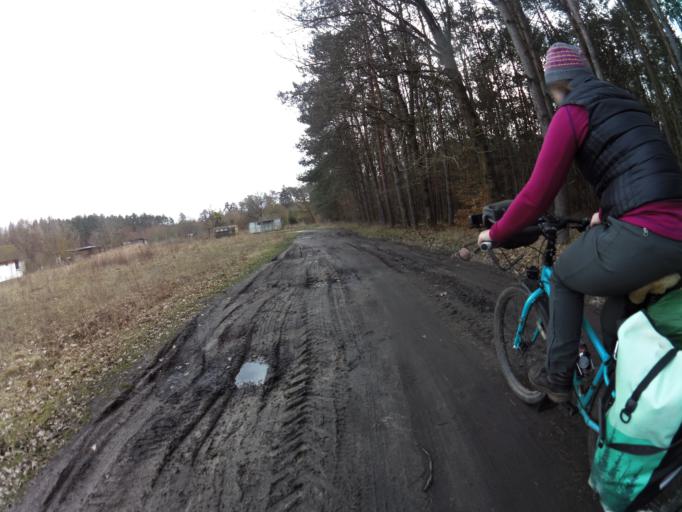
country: PL
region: Lubusz
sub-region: Powiat gorzowski
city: Lubiszyn
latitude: 52.7688
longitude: 14.8372
